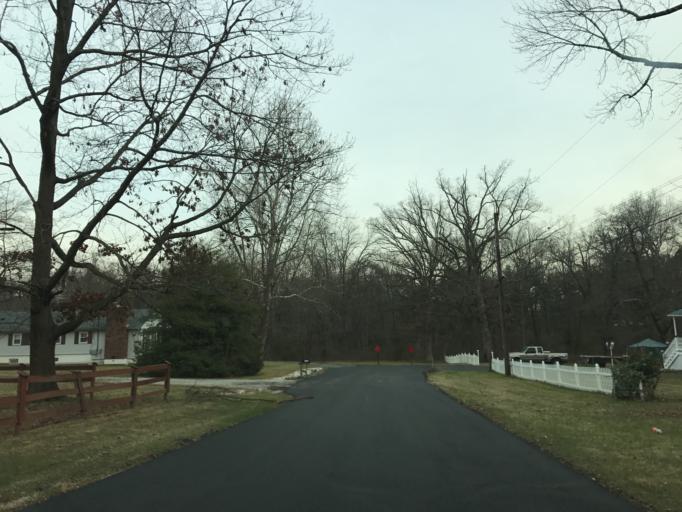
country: US
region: Maryland
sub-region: Baltimore County
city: White Marsh
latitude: 39.4089
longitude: -76.4054
